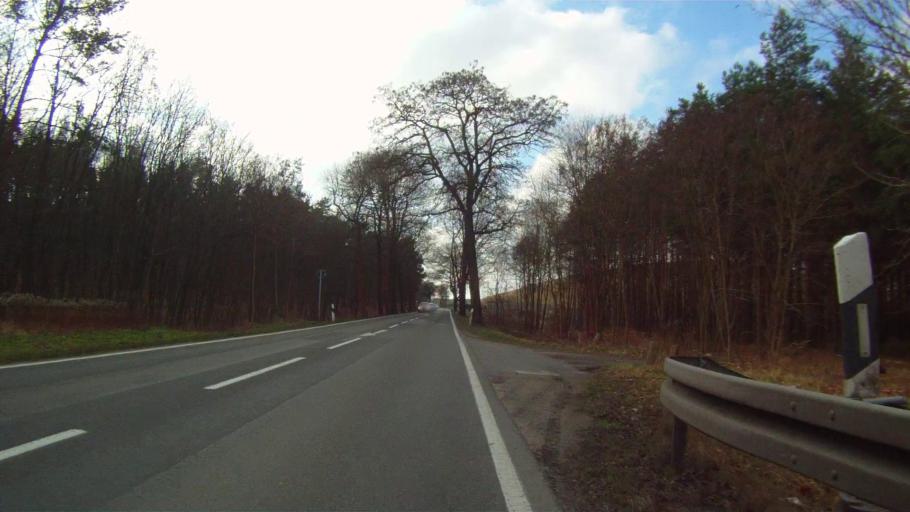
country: DE
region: Brandenburg
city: Erkner
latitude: 52.3859
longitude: 13.7310
